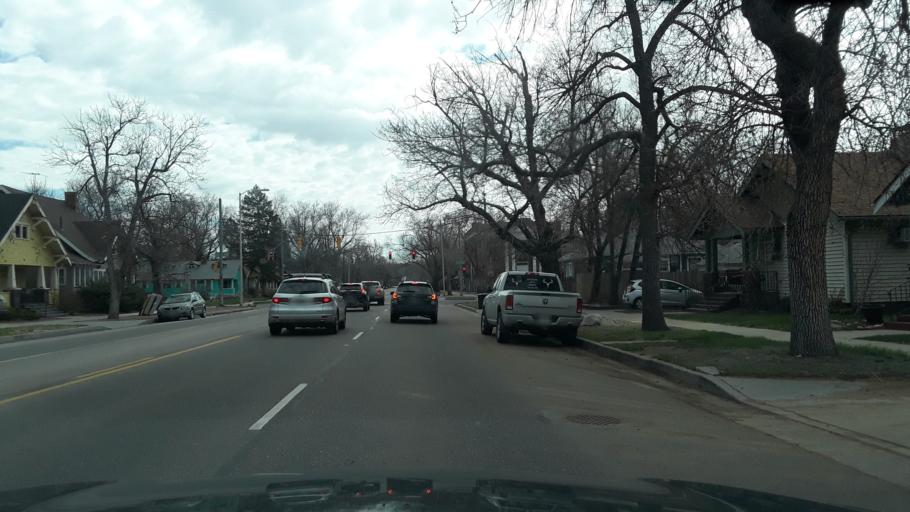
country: US
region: Colorado
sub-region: El Paso County
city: Colorado Springs
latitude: 38.8505
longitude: -104.8182
